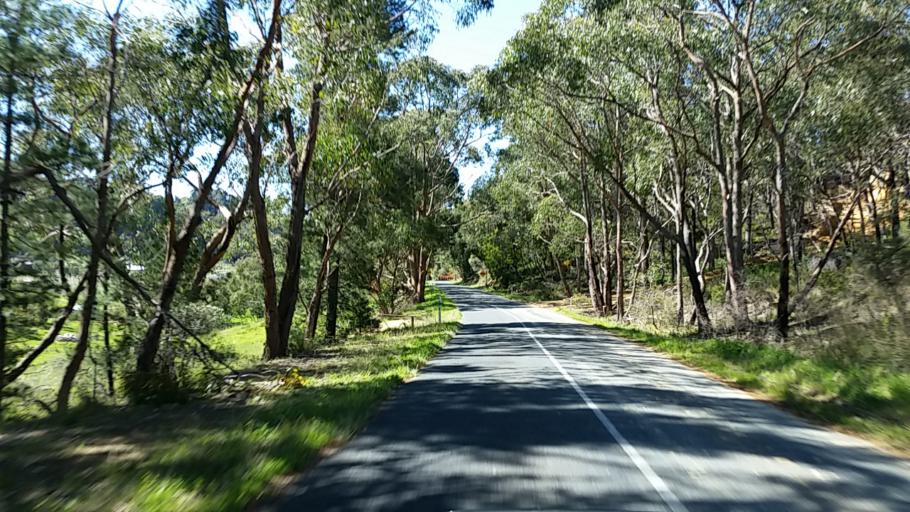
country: AU
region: South Australia
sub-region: Adelaide Hills
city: Bridgewater
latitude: -34.9464
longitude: 138.7650
